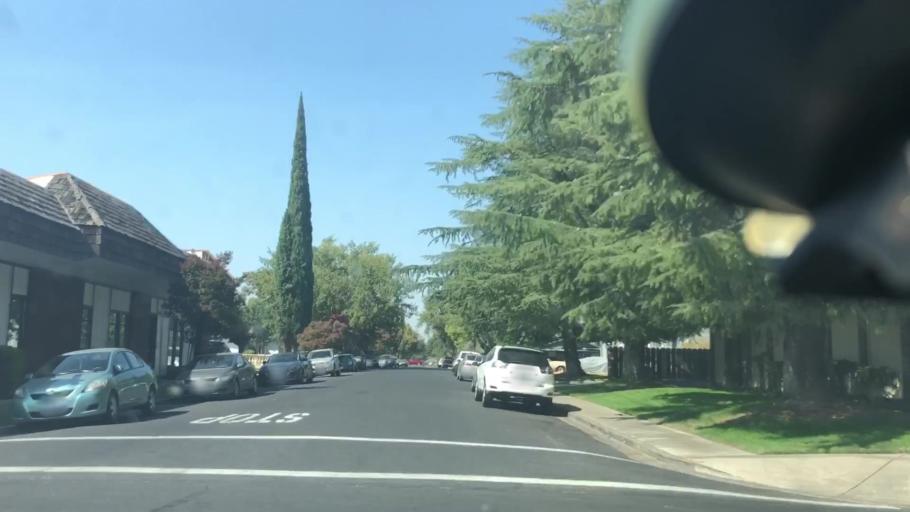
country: US
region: California
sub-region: San Joaquin County
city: Manteca
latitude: 37.7991
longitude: -121.2152
